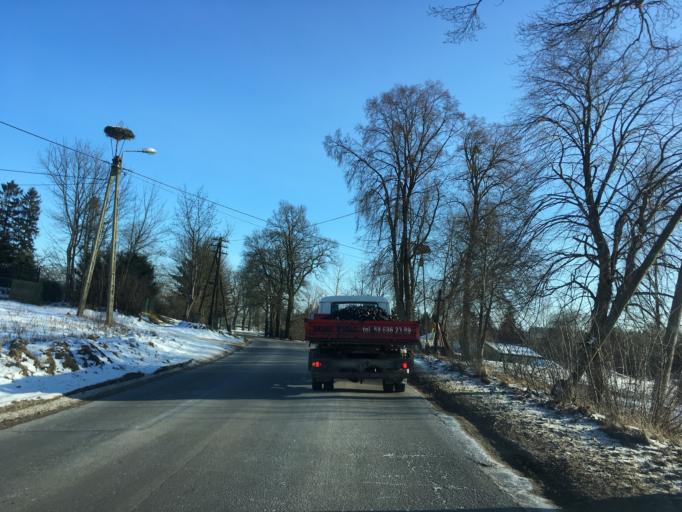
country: PL
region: Pomeranian Voivodeship
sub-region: Powiat koscierski
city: Koscierzyna
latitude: 54.0725
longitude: 18.0075
